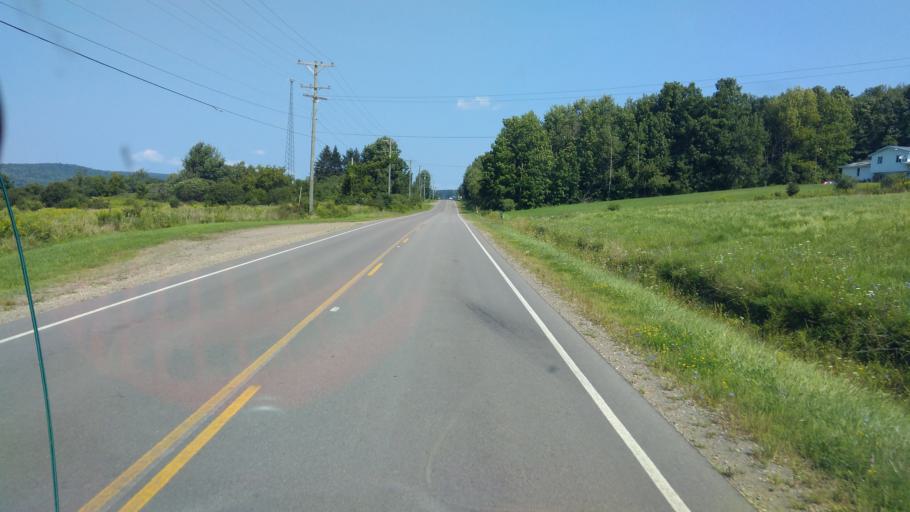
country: US
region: New York
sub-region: Allegany County
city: Belmont
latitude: 42.2919
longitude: -78.0262
